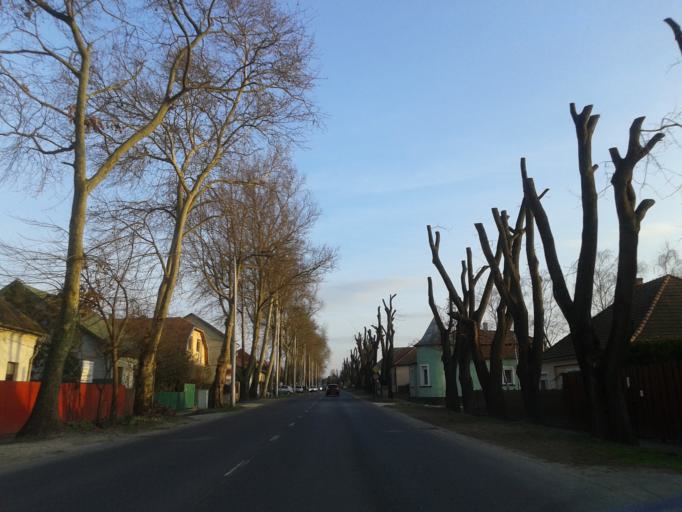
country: HU
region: Komarom-Esztergom
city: Tata
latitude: 47.6604
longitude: 18.3253
